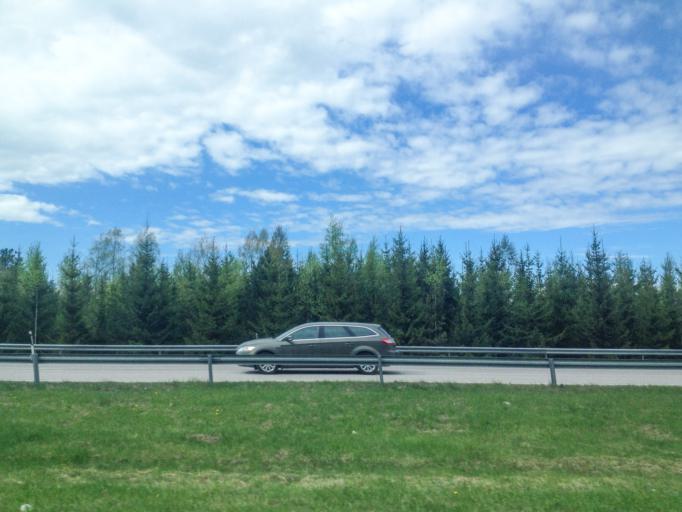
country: FI
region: Uusimaa
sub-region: Helsinki
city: Hyvinge
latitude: 60.6079
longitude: 24.8029
